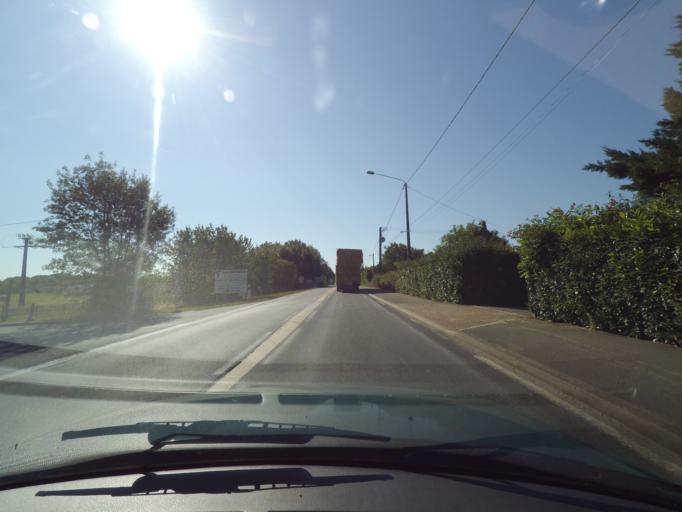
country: FR
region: Poitou-Charentes
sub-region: Departement de la Vienne
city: Lussac-les-Chateaux
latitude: 46.4077
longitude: 0.6930
